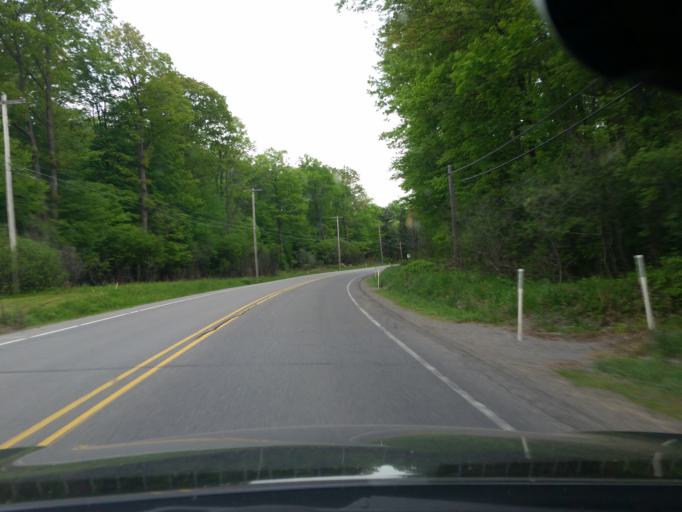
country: US
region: Pennsylvania
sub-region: Elk County
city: Ridgway
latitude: 41.3951
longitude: -78.6940
